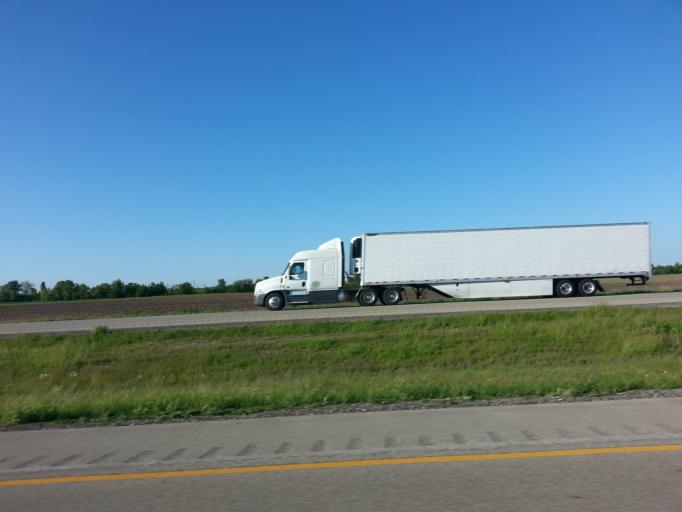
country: US
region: Illinois
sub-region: McLean County
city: Le Roy
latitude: 40.3575
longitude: -88.8056
